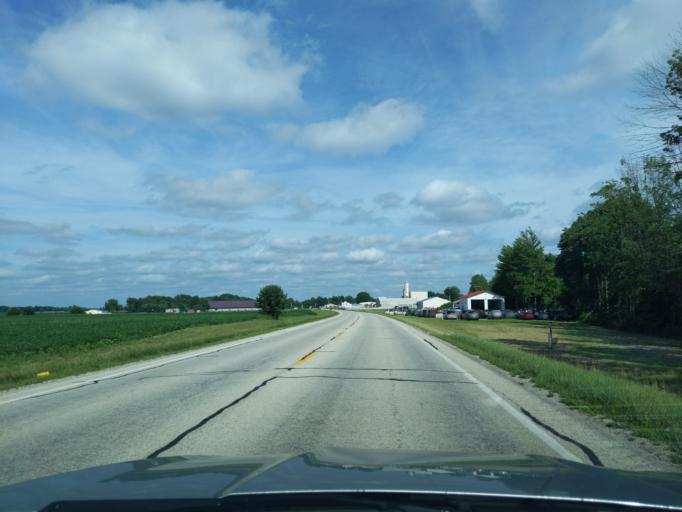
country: US
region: Indiana
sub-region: Ripley County
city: Batesville
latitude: 39.3113
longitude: -85.3421
